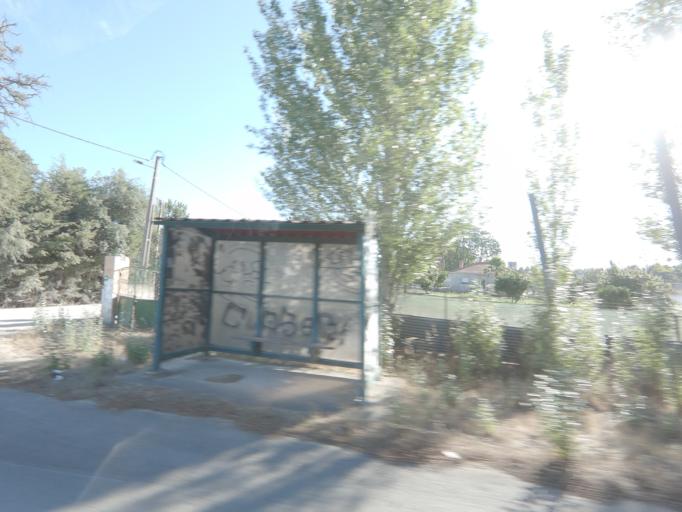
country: PT
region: Setubal
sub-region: Palmela
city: Pinhal Novo
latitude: 38.6151
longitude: -8.9520
